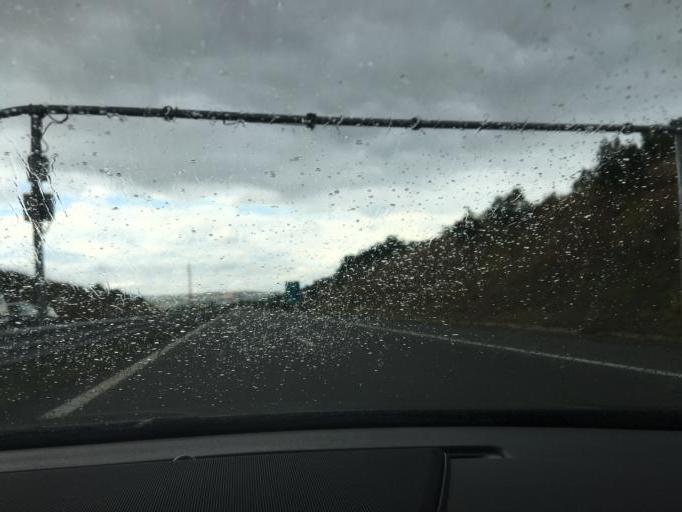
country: BG
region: Kyustendil
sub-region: Obshtina Bobovdol
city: Bobovdol
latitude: 42.3464
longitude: 23.0954
